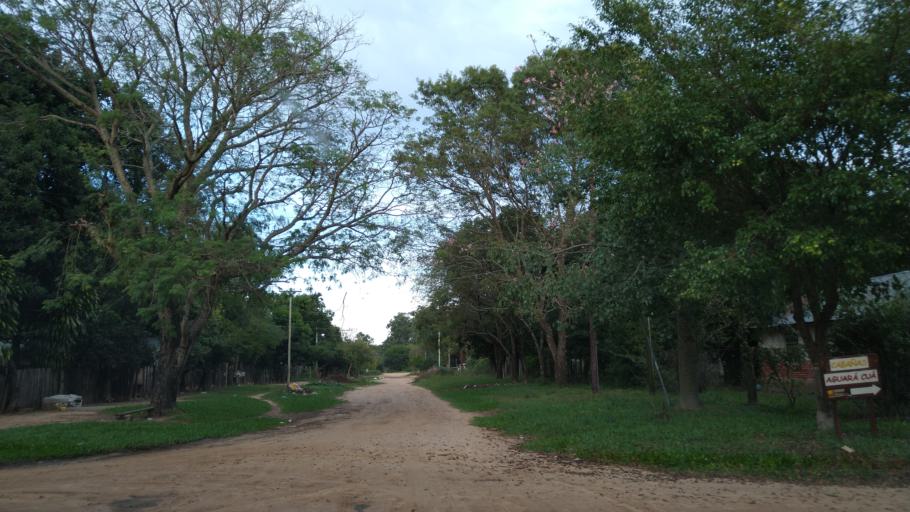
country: AR
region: Corrientes
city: Ituzaingo
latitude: -27.5939
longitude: -56.7078
